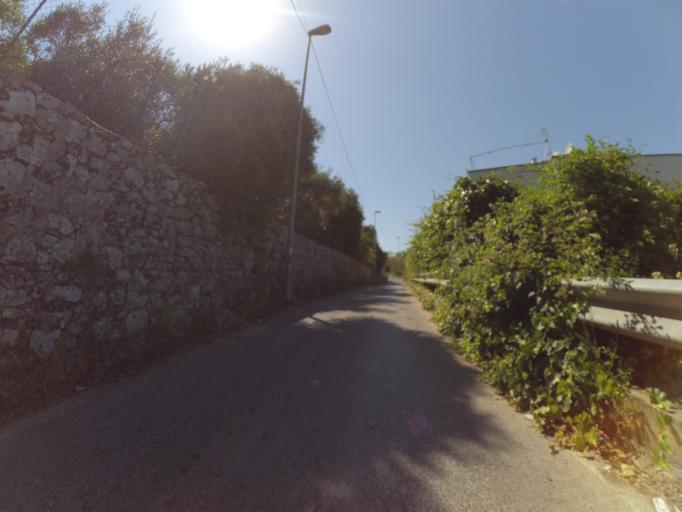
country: IT
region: Latium
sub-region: Provincia di Latina
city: Gaeta
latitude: 41.2185
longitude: 13.5566
